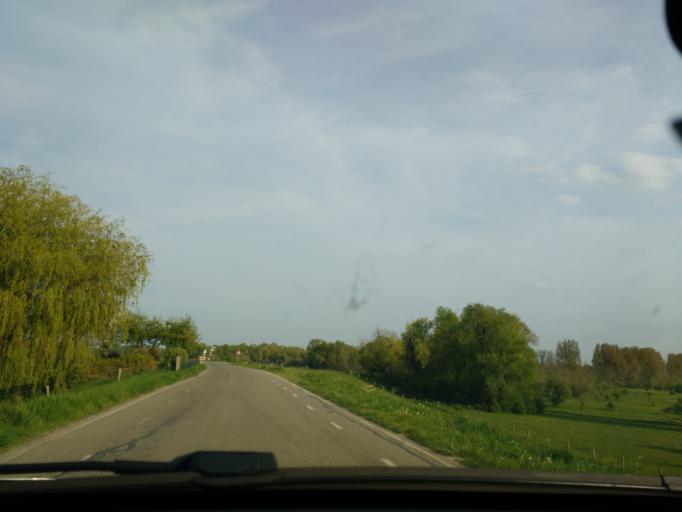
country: NL
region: Utrecht
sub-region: Gemeente Rhenen
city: Rhenen
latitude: 51.9491
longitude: 5.6176
